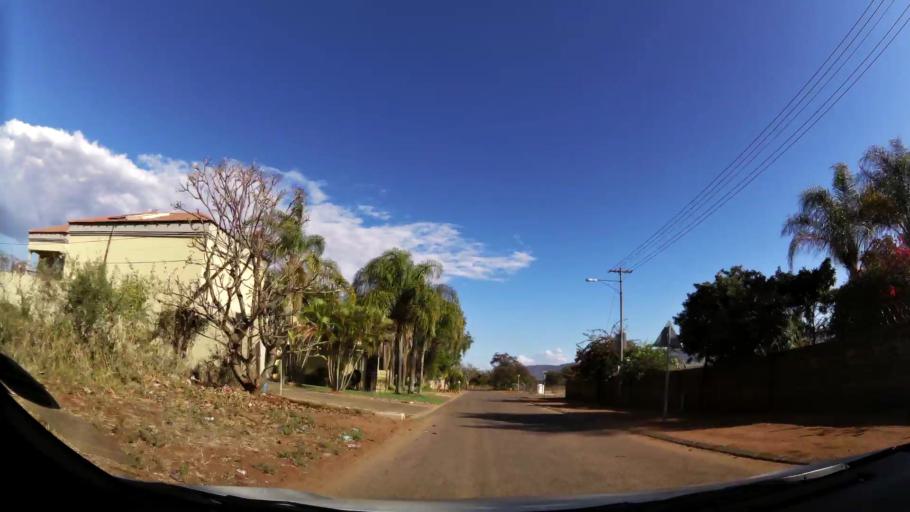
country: ZA
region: Limpopo
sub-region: Waterberg District Municipality
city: Mokopane
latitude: -24.1801
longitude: 28.9974
